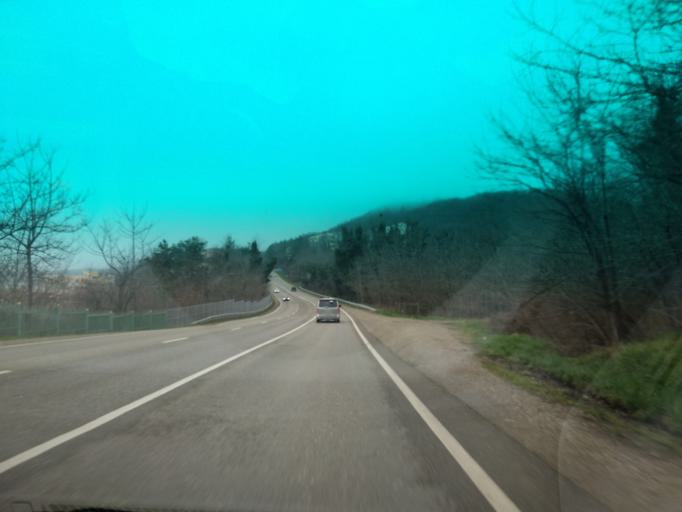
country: RU
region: Krasnodarskiy
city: Ol'ginka
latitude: 44.1774
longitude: 38.9418
